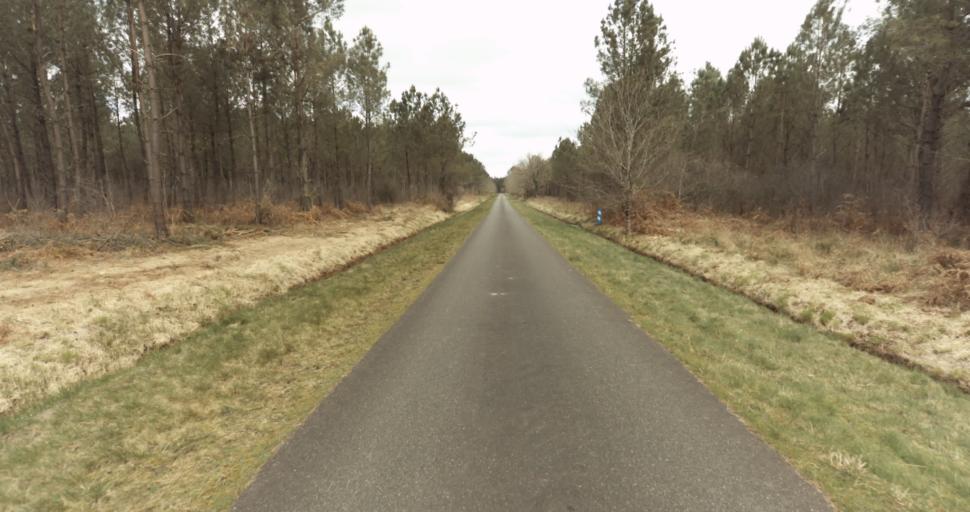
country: FR
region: Aquitaine
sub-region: Departement des Landes
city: Roquefort
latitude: 44.1050
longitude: -0.4541
